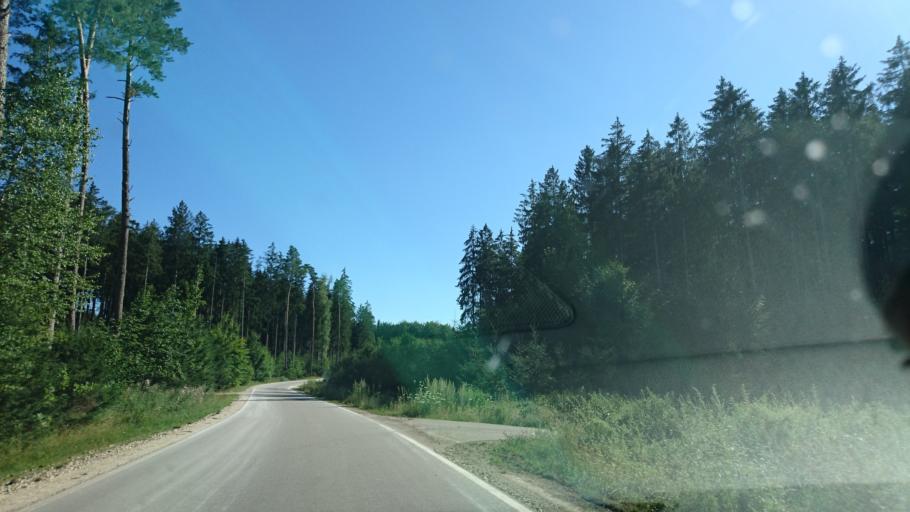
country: DE
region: Bavaria
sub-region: Swabia
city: Heretsried
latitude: 48.4524
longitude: 10.7738
